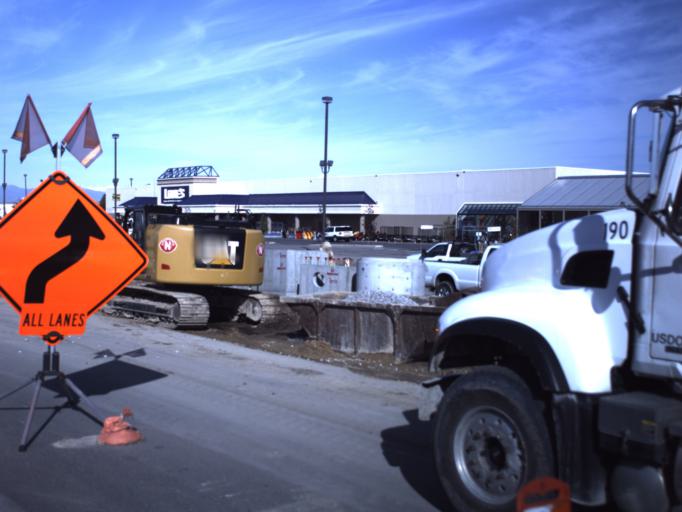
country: US
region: Utah
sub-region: Utah County
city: Orem
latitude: 40.2736
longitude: -111.6972
